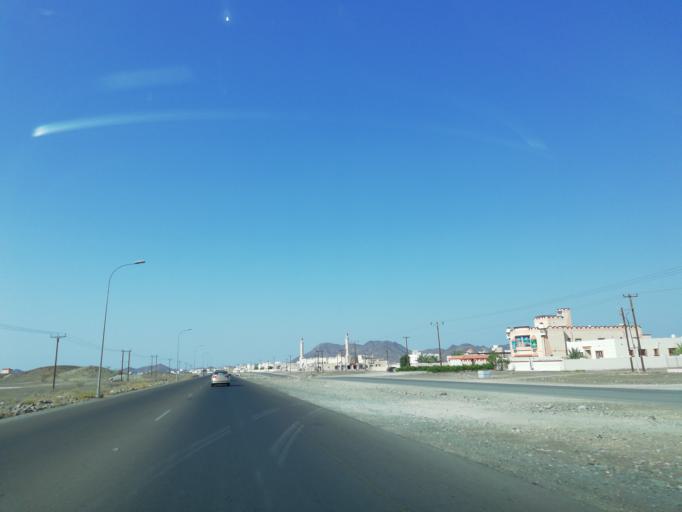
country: OM
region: Ash Sharqiyah
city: Ibra'
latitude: 22.7868
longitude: 58.1455
